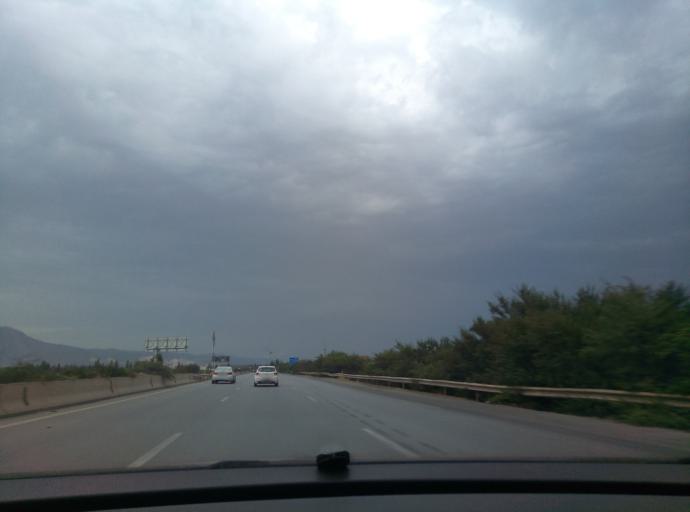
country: TN
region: Tunis
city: Rades
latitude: 36.7210
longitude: 10.2628
